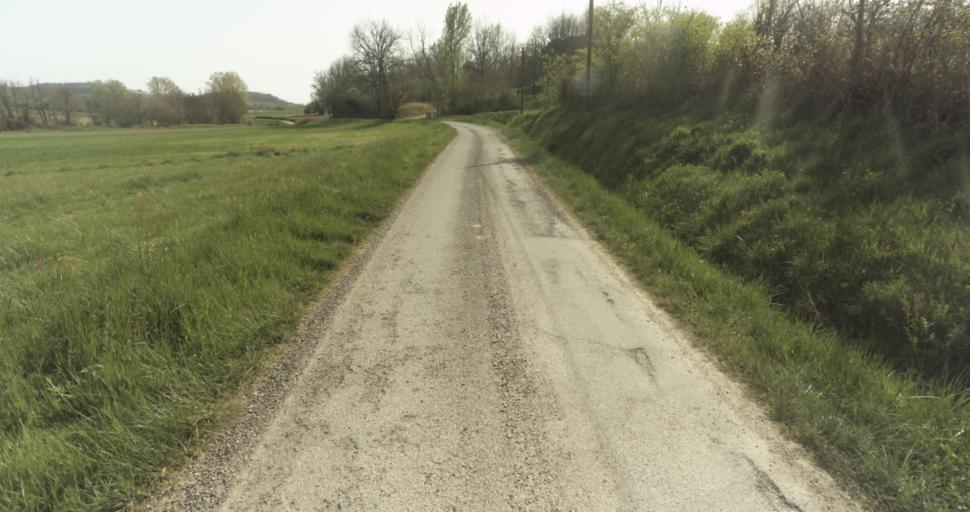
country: FR
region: Midi-Pyrenees
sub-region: Departement du Tarn-et-Garonne
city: Moissac
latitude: 44.1397
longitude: 1.1590
